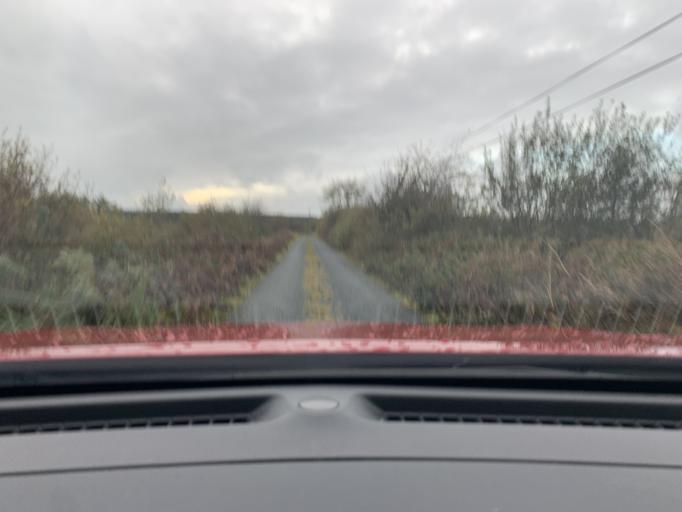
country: IE
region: Connaught
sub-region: Roscommon
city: Ballaghaderreen
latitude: 53.9687
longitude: -8.5921
